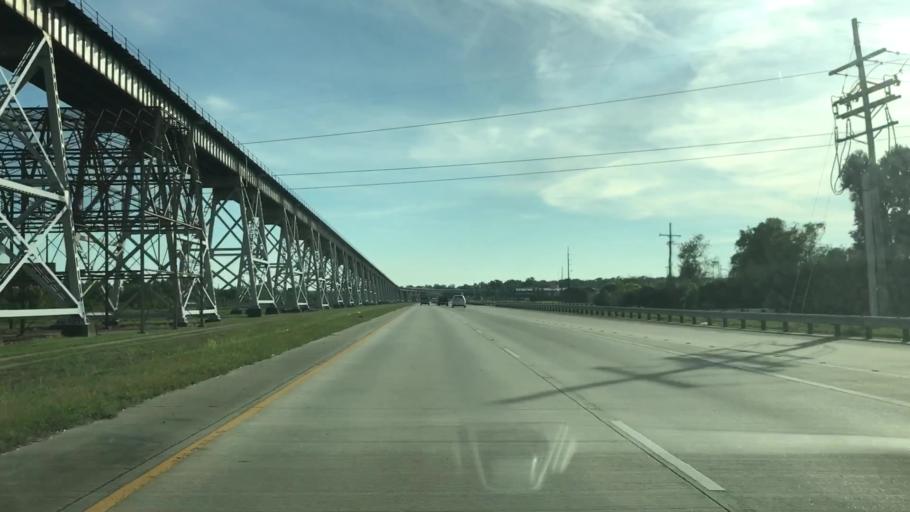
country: US
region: Louisiana
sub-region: Jefferson Parish
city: Bridge City
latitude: 29.9255
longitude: -90.1676
